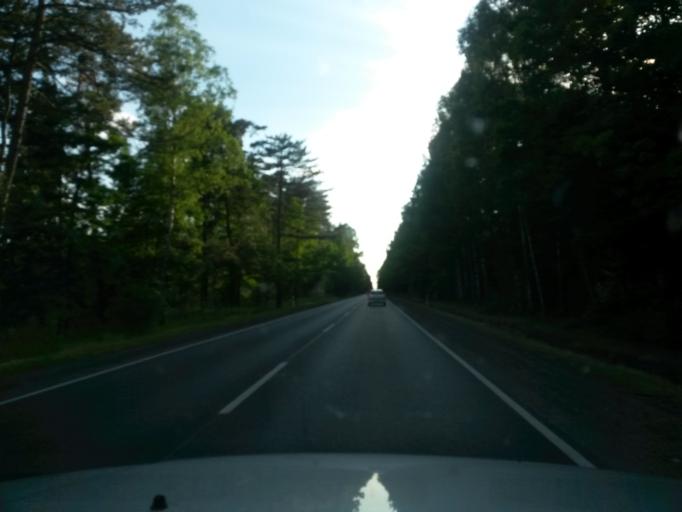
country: PL
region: Lodz Voivodeship
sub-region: Powiat belchatowski
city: Kluki
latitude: 51.3408
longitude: 19.2090
